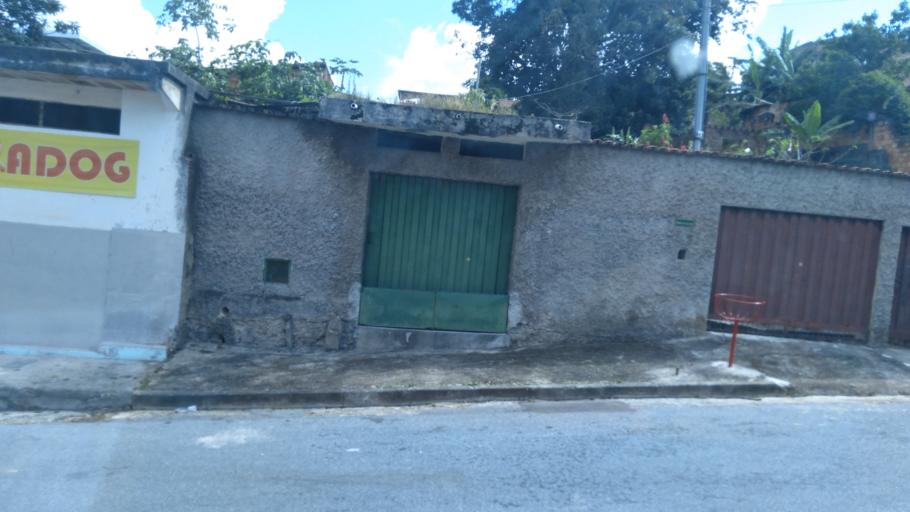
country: BR
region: Minas Gerais
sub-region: Belo Horizonte
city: Belo Horizonte
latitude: -19.8615
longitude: -43.9018
